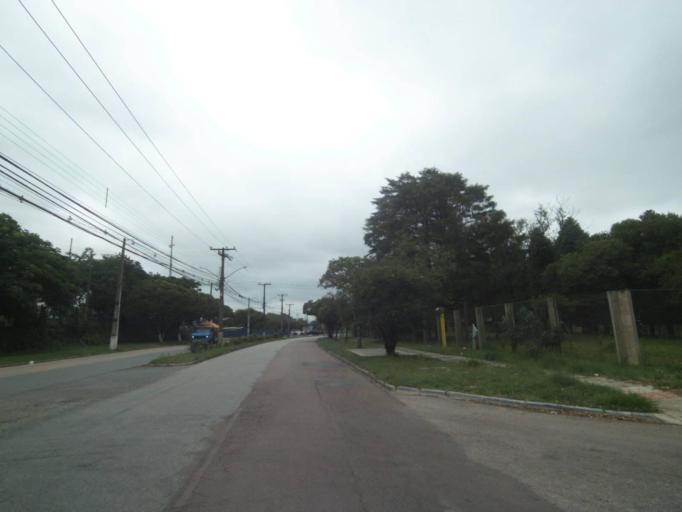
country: BR
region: Parana
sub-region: Sao Jose Dos Pinhais
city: Sao Jose dos Pinhais
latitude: -25.5536
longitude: -49.3092
